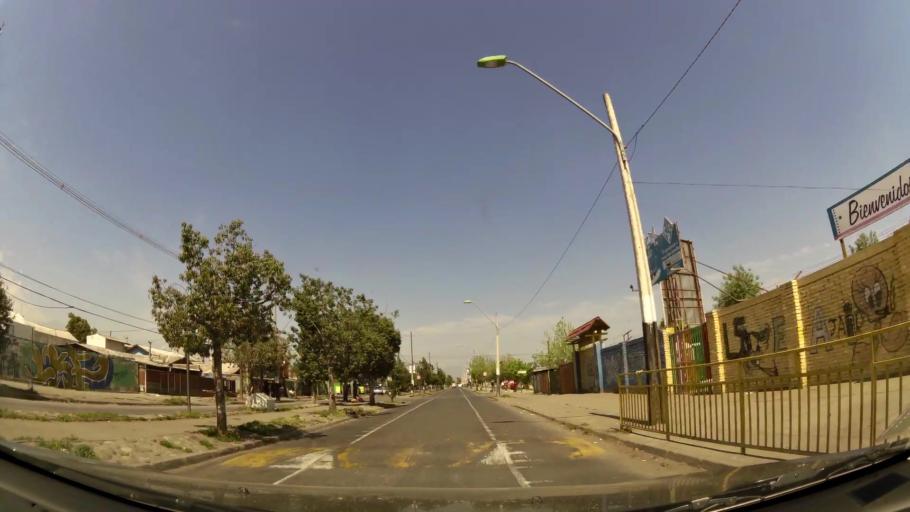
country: CL
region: Santiago Metropolitan
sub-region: Provincia de Santiago
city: La Pintana
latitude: -33.5878
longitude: -70.6193
